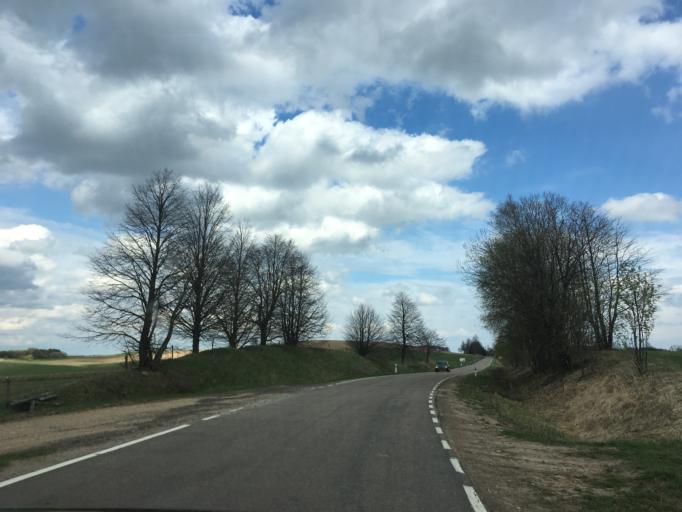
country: LT
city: Virbalis
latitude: 54.3648
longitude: 22.8364
